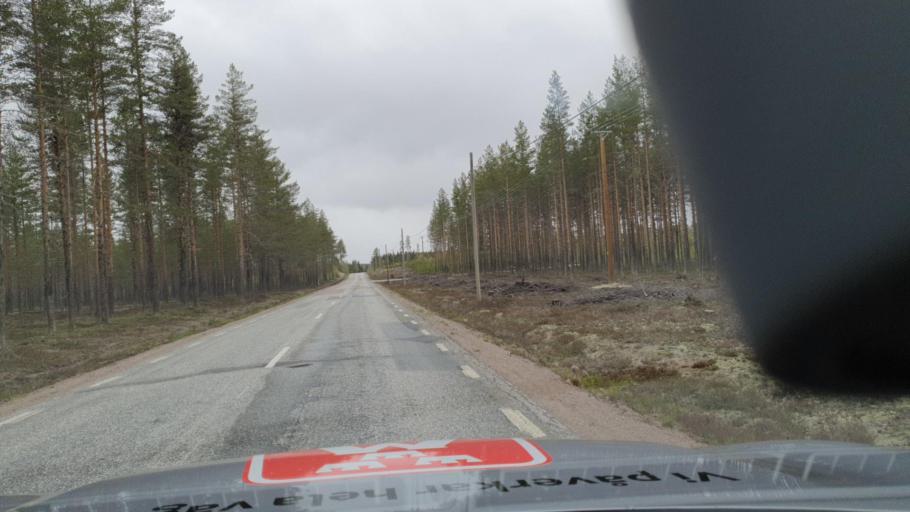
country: SE
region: Vaesternorrland
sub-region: Solleftea Kommun
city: Solleftea
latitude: 63.6034
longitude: 17.5372
